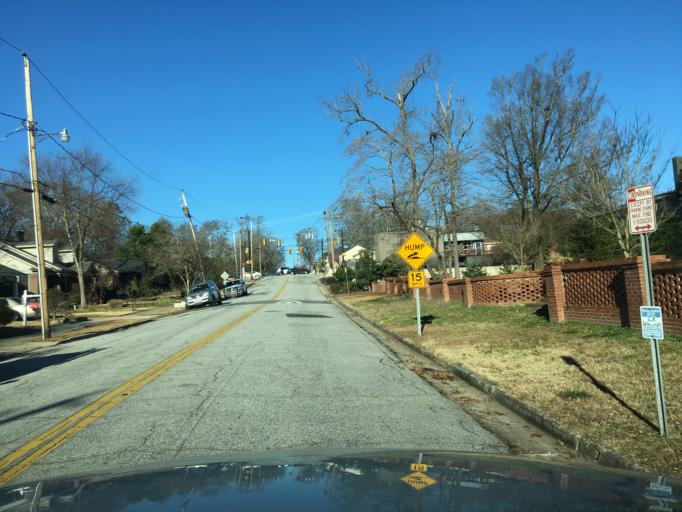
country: US
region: South Carolina
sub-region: Greenville County
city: Greenville
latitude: 34.8593
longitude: -82.3902
